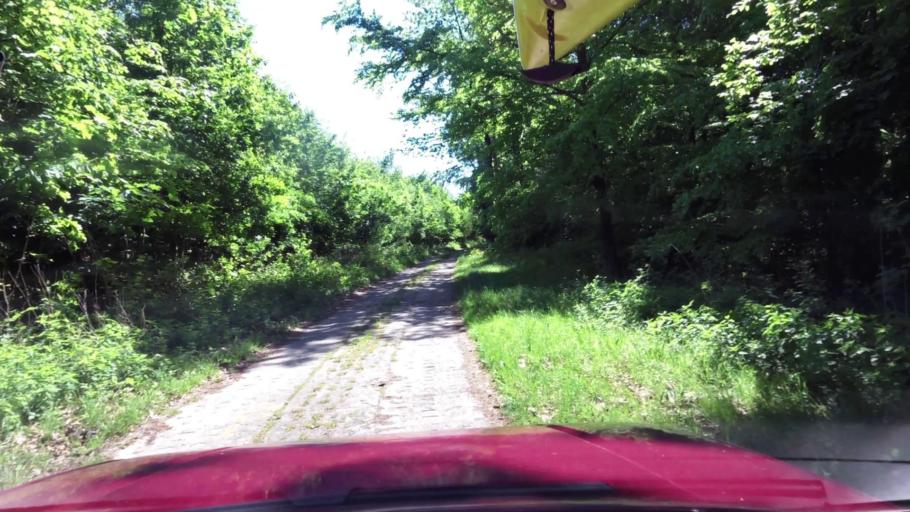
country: PL
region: West Pomeranian Voivodeship
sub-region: Powiat koszalinski
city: Polanow
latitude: 54.0336
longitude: 16.7957
